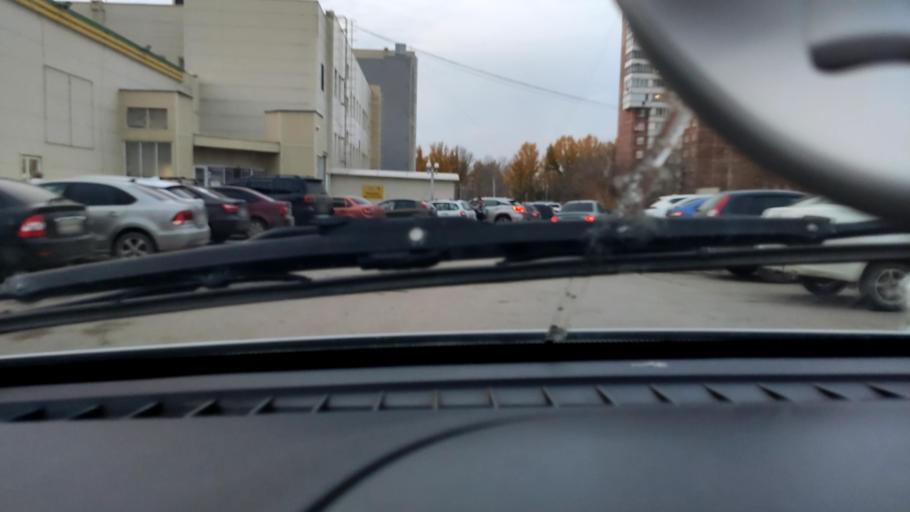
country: RU
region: Perm
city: Perm
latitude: 57.9773
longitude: 56.1905
